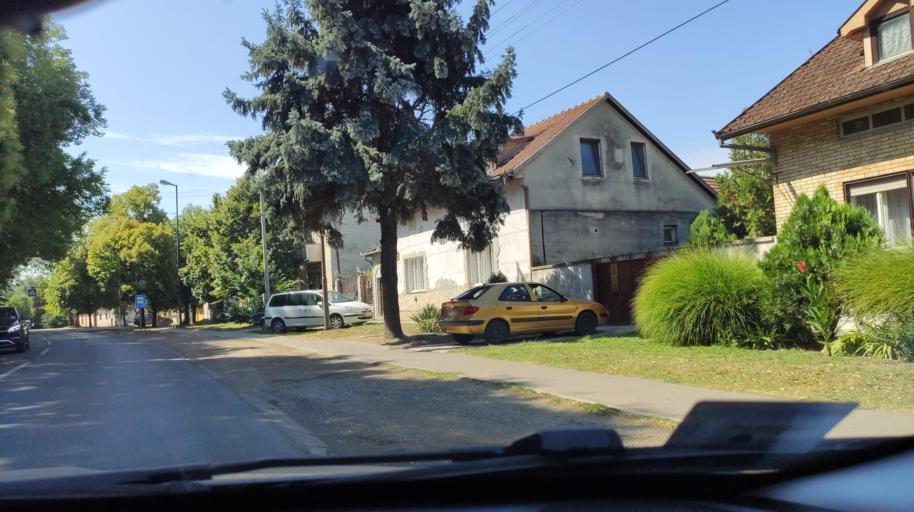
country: RS
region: Autonomna Pokrajina Vojvodina
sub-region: Severnobacki Okrug
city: Backa Topola
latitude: 45.8177
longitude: 19.6292
